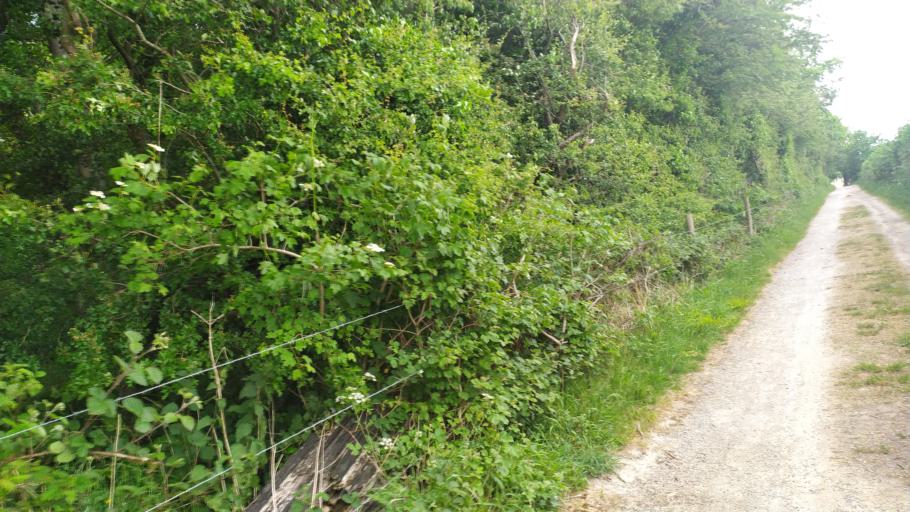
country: GB
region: England
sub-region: City and Borough of Leeds
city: Thorner
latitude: 53.8586
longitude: -1.3912
